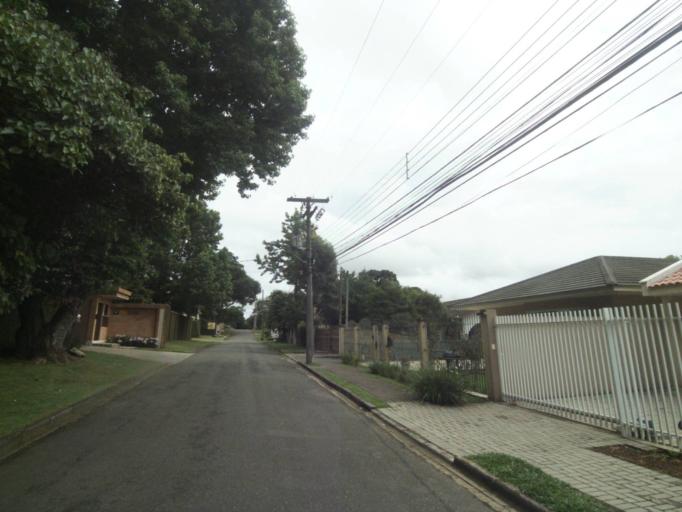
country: BR
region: Parana
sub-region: Curitiba
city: Curitiba
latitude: -25.4474
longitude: -49.3377
